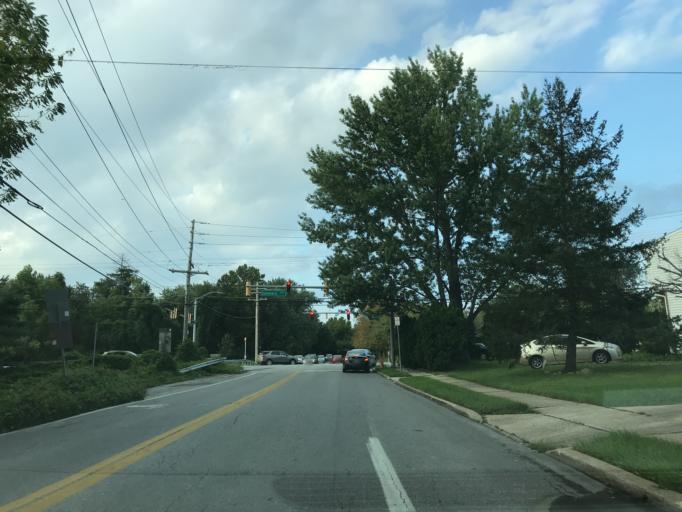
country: US
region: Maryland
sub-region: Baltimore County
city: Mays Chapel
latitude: 39.4242
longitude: -76.6486
